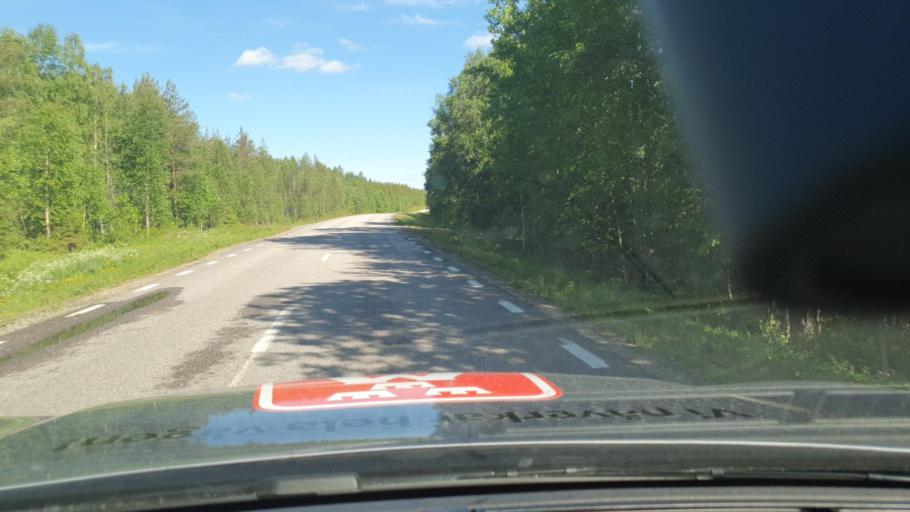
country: SE
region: Norrbotten
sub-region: Overkalix Kommun
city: OEverkalix
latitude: 66.6584
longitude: 22.6886
